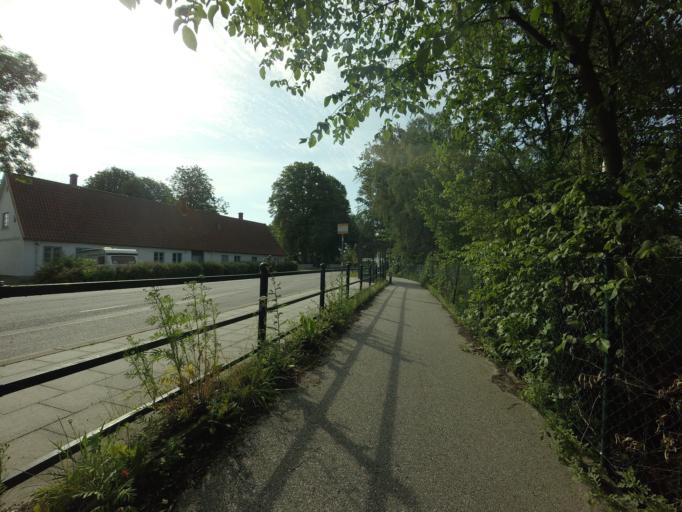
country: SE
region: Skane
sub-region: Malmo
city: Tygelsjo
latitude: 55.5021
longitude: 12.9951
